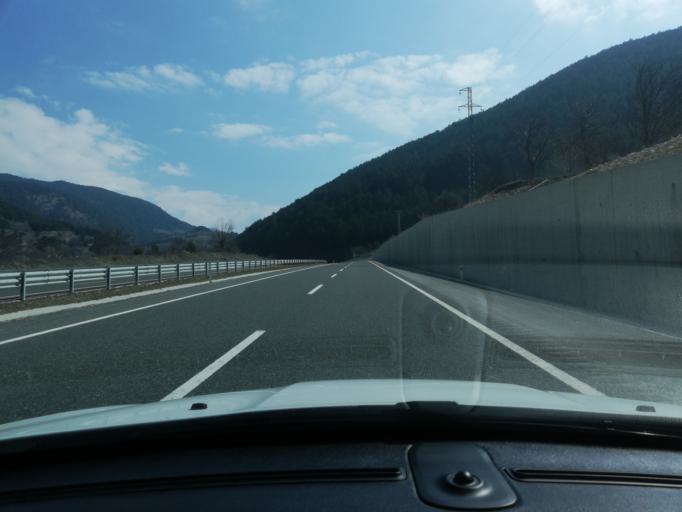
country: TR
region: Cankiri
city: Ilgaz
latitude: 41.0286
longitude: 33.7322
